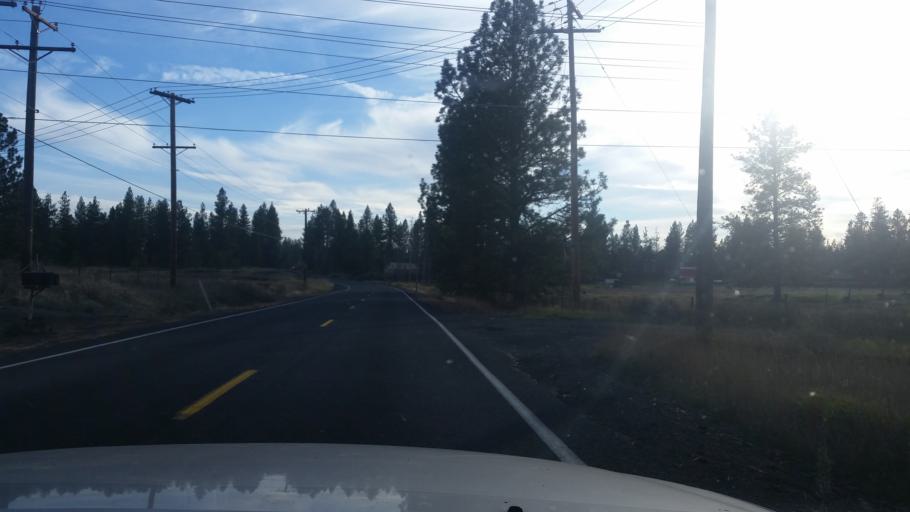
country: US
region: Washington
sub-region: Spokane County
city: Cheney
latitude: 47.4771
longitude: -117.5805
